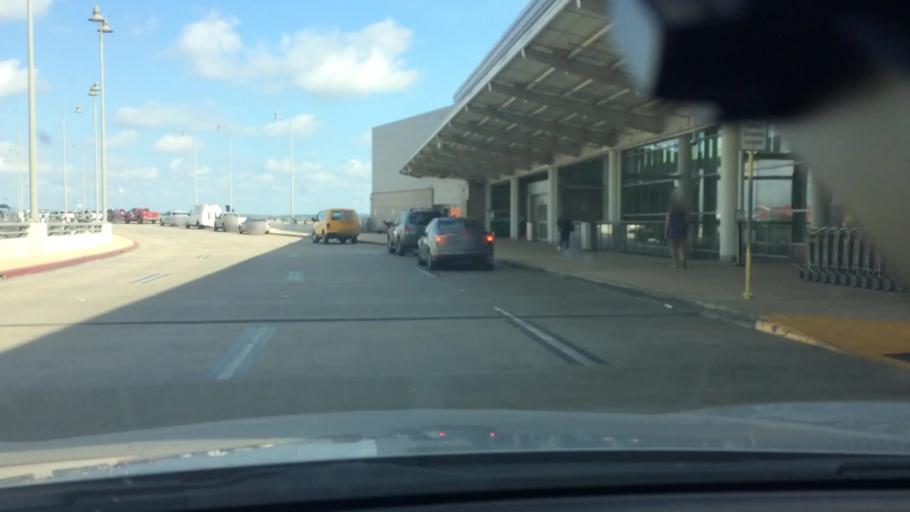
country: US
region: Texas
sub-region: Bexar County
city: Alamo Heights
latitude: 29.5274
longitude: -98.4730
